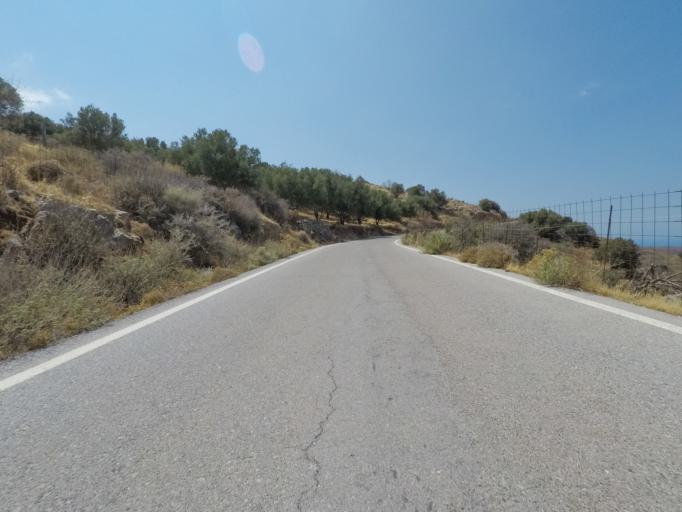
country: GR
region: Crete
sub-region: Nomos Lasithiou
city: Elounda
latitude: 35.3190
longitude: 25.6753
